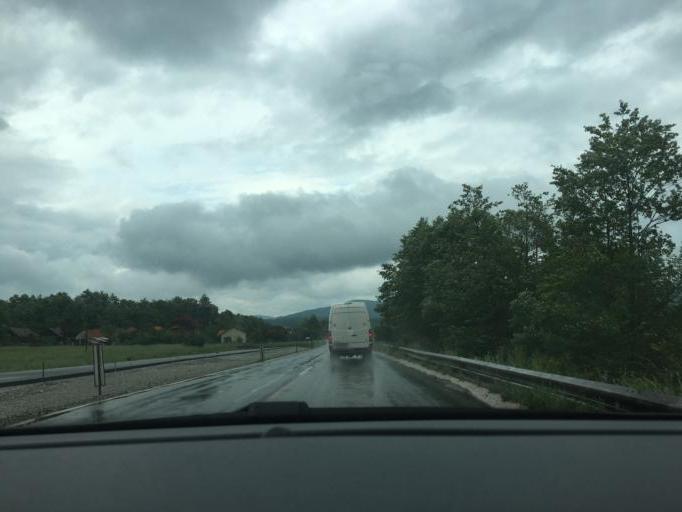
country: MK
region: Debarca
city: Belcista
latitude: 41.3283
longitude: 20.7969
